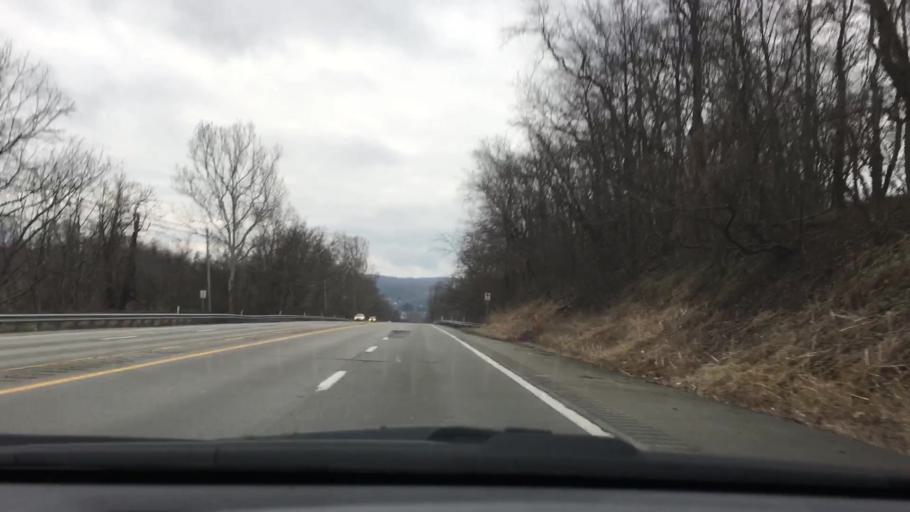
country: US
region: Pennsylvania
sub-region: Fayette County
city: Perryopolis
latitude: 40.1041
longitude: -79.7682
